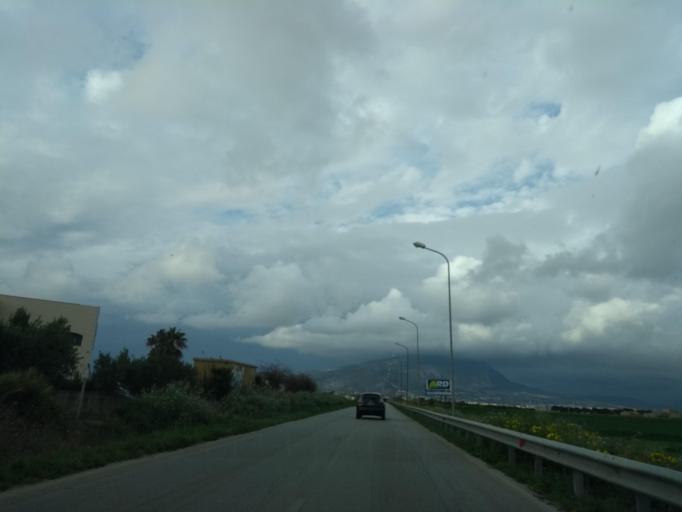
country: IT
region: Sicily
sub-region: Trapani
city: Paceco
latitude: 37.9748
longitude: 12.5263
